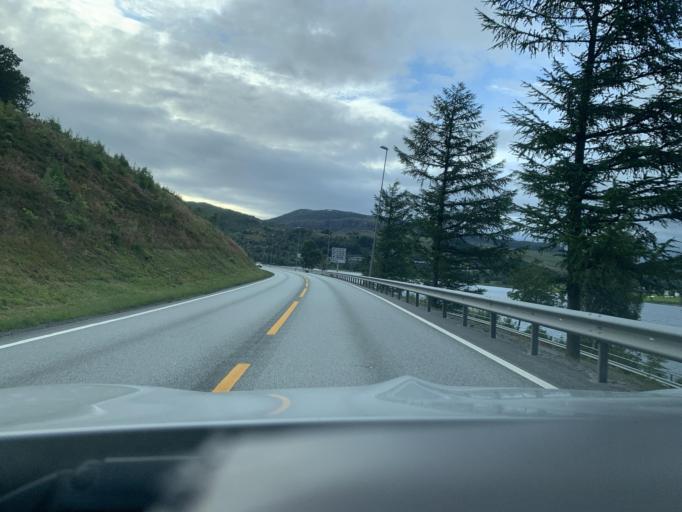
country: NO
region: Rogaland
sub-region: Bjerkreim
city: Vikesa
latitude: 58.6267
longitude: 6.0903
